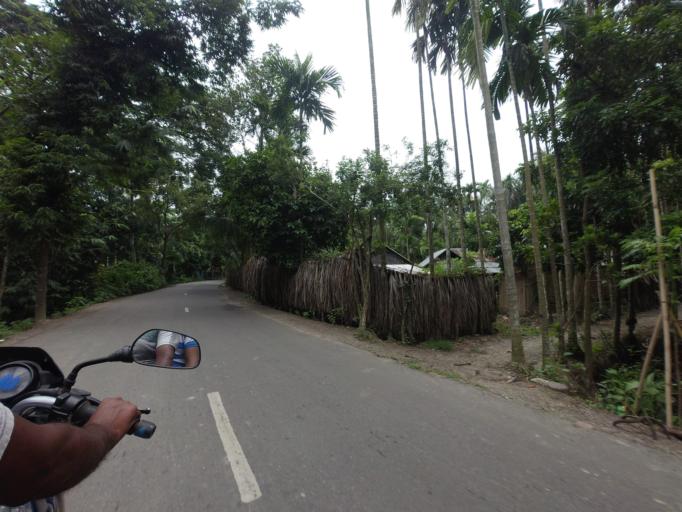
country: BD
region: Khulna
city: Kalia
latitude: 23.1572
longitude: 89.6440
